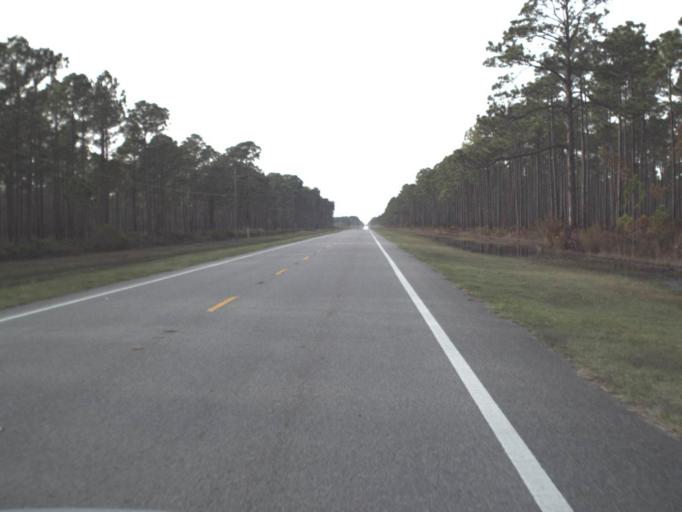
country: US
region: Florida
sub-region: Bay County
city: Mexico Beach
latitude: 30.0125
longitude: -85.5157
